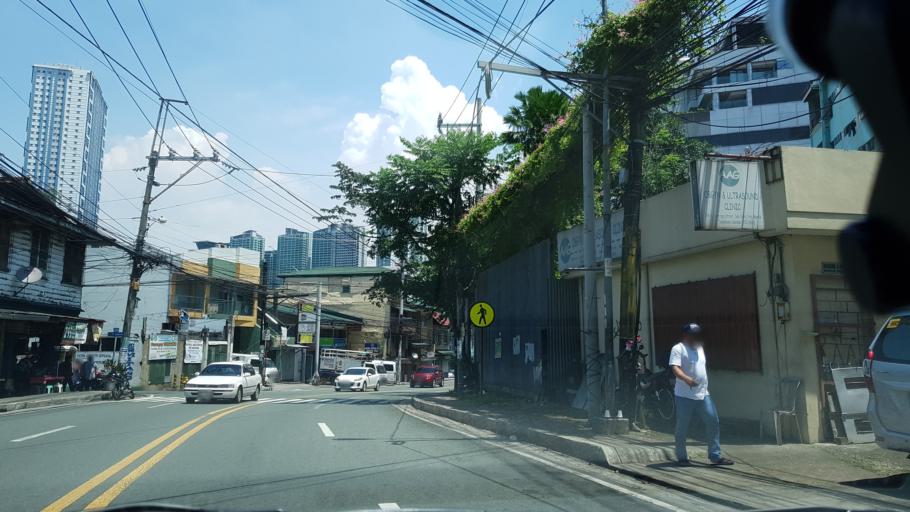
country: PH
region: Metro Manila
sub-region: San Juan
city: San Juan
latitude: 14.6104
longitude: 121.0311
